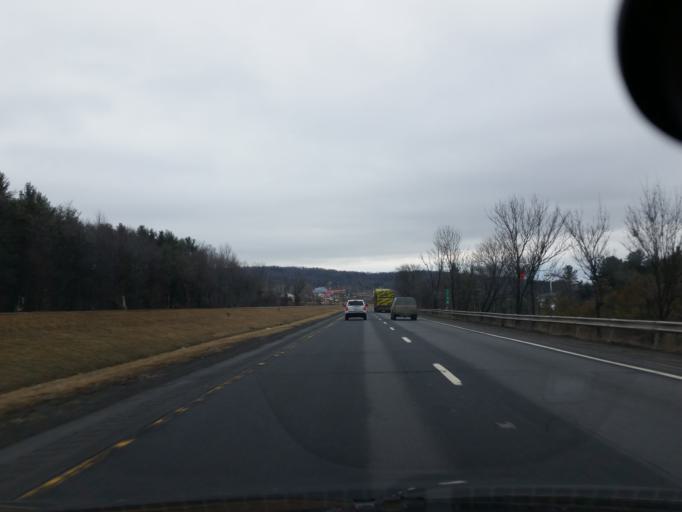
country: US
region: Pennsylvania
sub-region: Susquehanna County
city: Susquehanna
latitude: 41.8311
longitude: -75.6806
